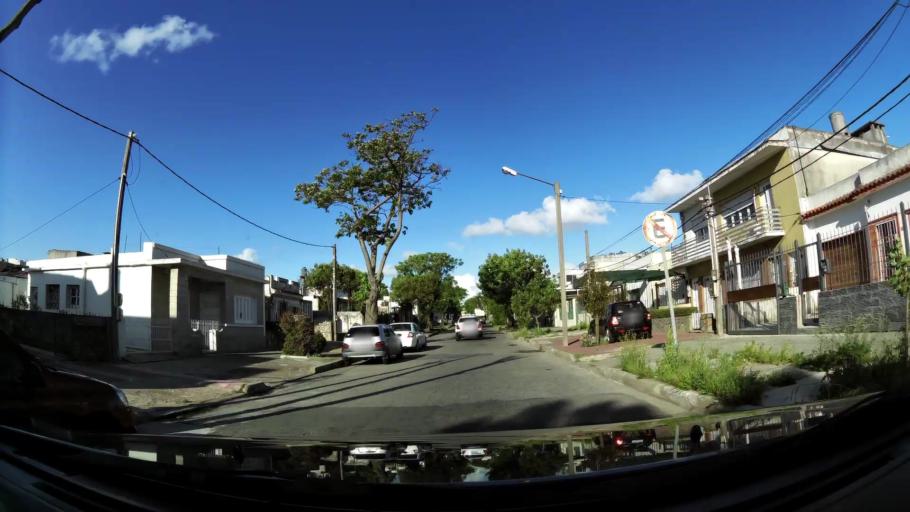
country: UY
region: Montevideo
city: Montevideo
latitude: -34.8789
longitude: -56.1515
